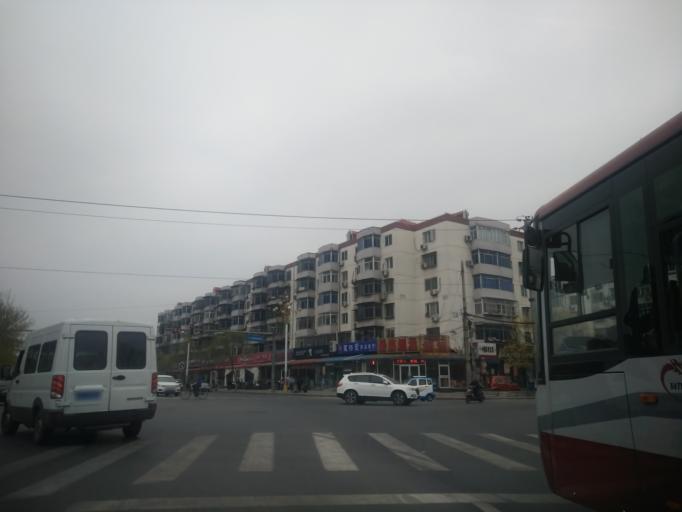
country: CN
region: Beijing
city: Jiugong
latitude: 39.8057
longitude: 116.4502
